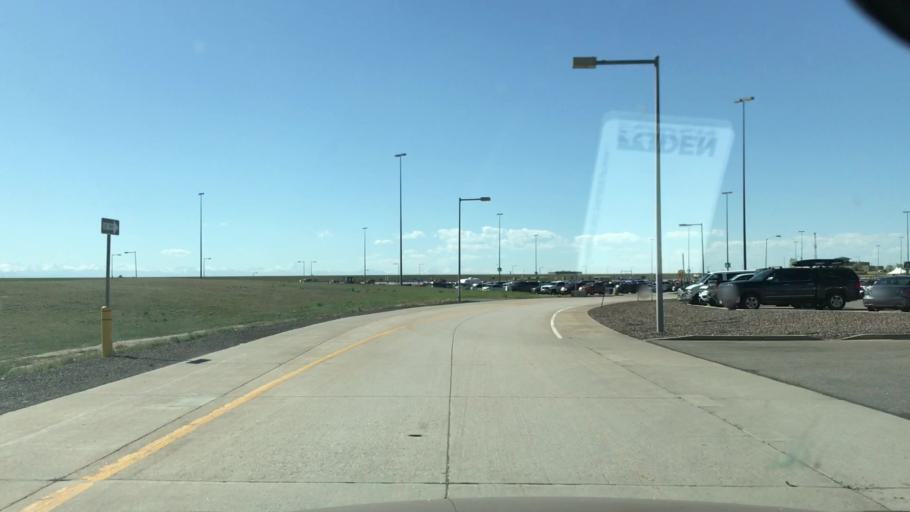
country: US
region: Colorado
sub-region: Weld County
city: Lochbuie
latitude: 39.8451
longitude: -104.6785
